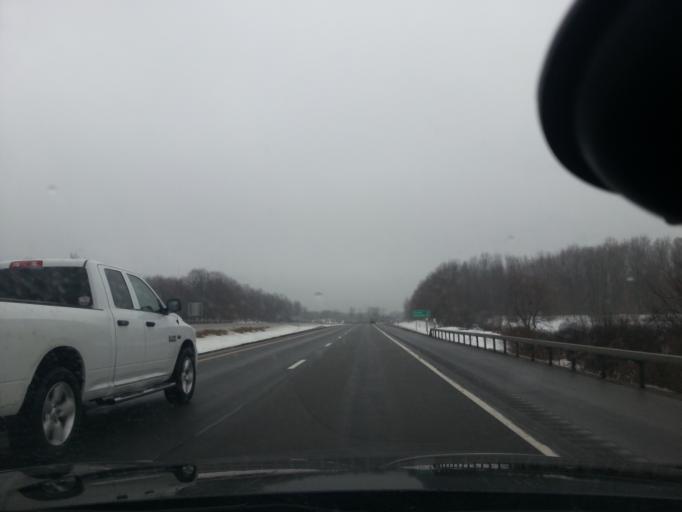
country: US
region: New York
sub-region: Oswego County
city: Pulaski
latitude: 43.6332
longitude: -76.0818
